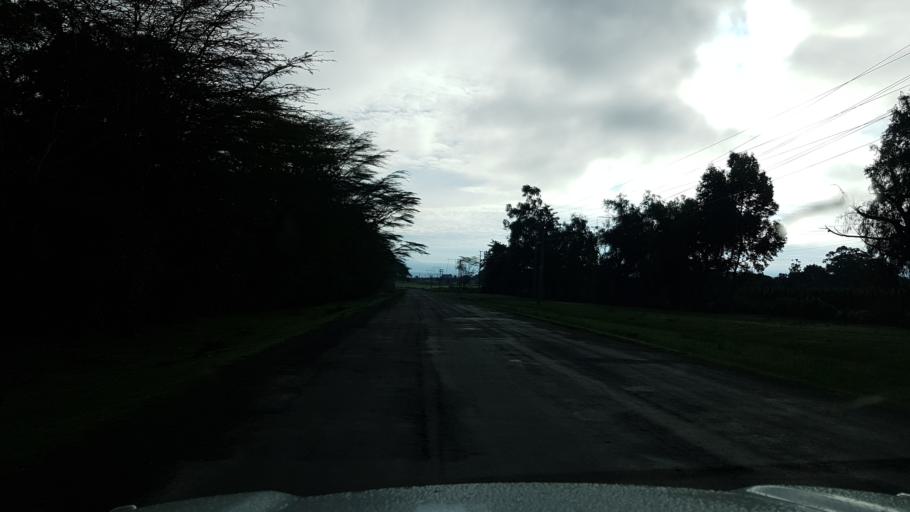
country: KE
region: Nakuru
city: Naivasha
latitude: -0.8249
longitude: 36.3798
